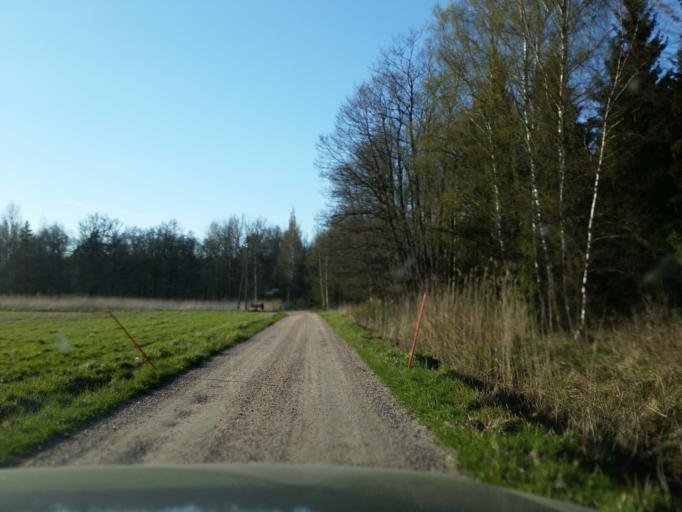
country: FI
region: Uusimaa
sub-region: Helsinki
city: Espoo
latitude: 60.1164
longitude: 24.6152
